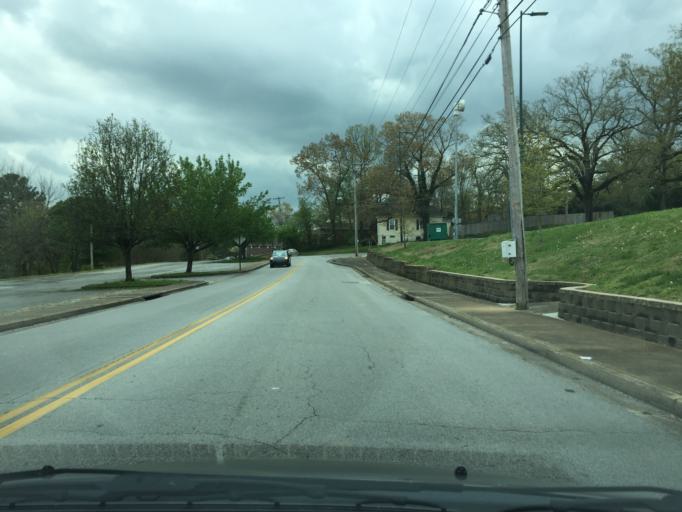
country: US
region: Tennessee
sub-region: Hamilton County
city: Falling Water
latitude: 35.1449
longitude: -85.2391
